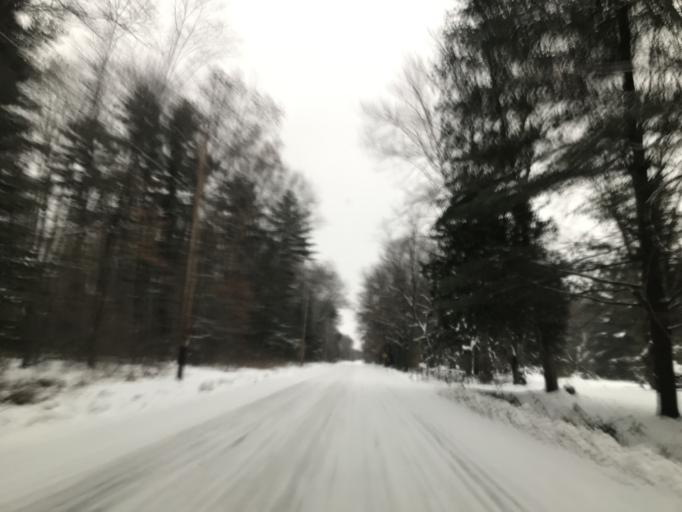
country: US
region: Wisconsin
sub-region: Marinette County
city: Peshtigo
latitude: 45.0440
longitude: -87.7194
